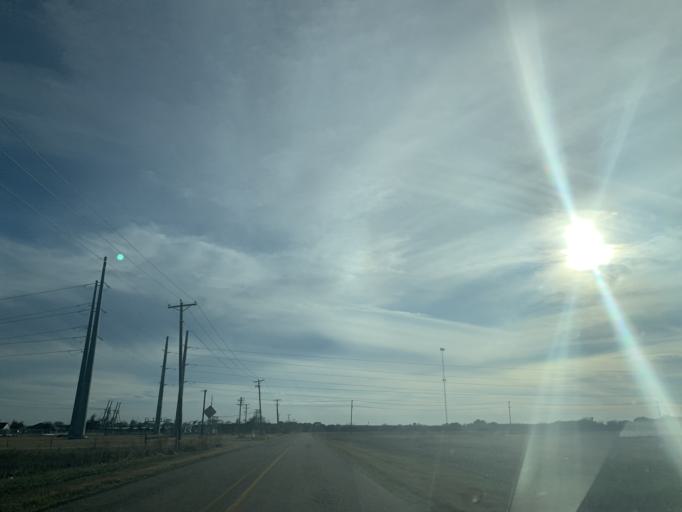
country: US
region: Texas
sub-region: Bell County
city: Salado
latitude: 30.9738
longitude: -97.5128
